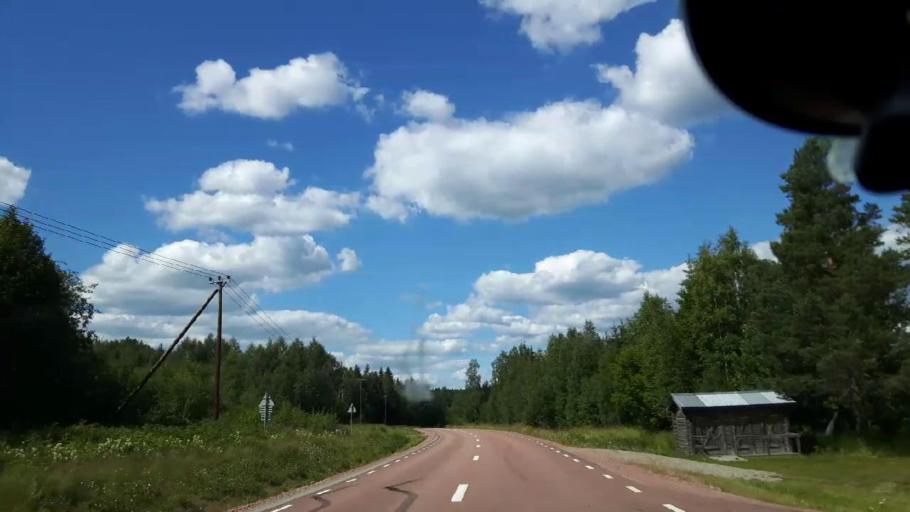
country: SE
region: Jaemtland
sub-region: Ragunda Kommun
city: Hammarstrand
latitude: 63.0137
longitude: 16.6244
